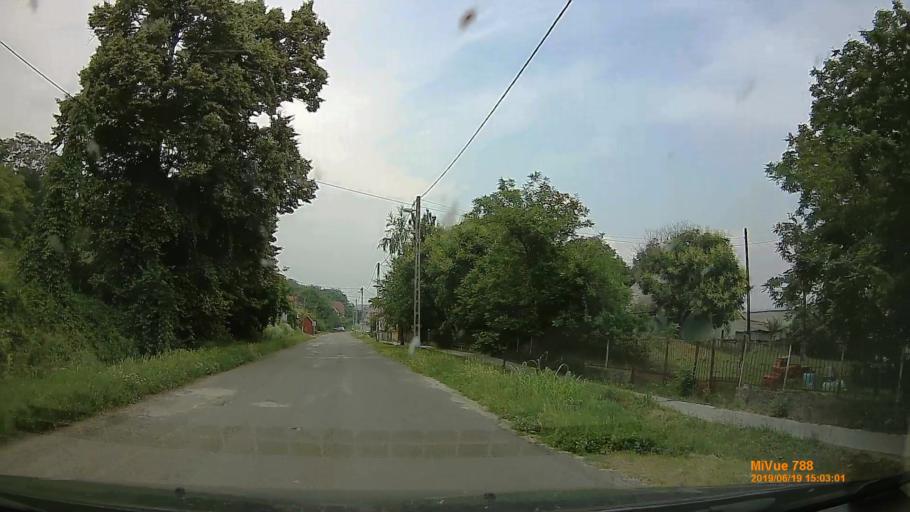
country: HU
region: Baranya
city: Szigetvar
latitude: 46.0921
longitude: 17.8051
